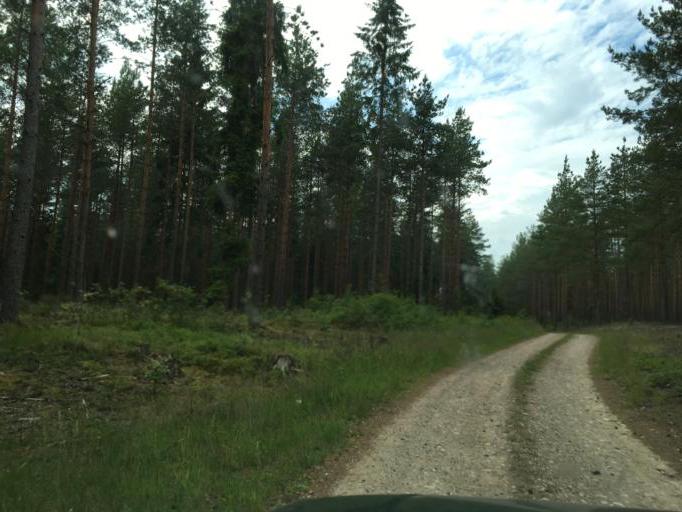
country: LV
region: Vilanu
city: Vilani
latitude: 56.7188
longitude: 26.9423
